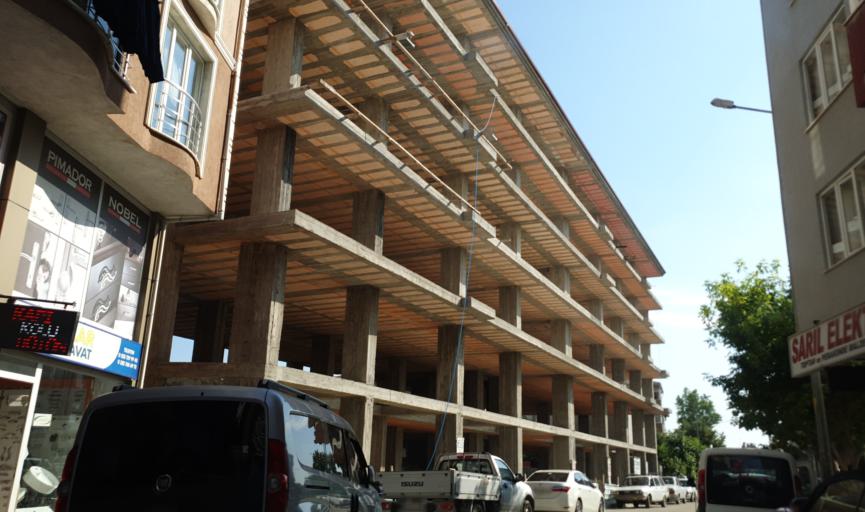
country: TR
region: Tekirdag
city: Saray
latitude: 41.4407
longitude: 27.9192
